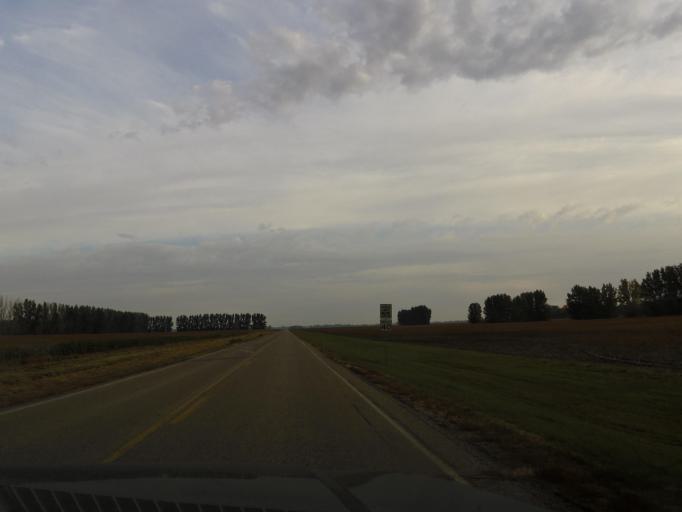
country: US
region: North Dakota
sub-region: Pembina County
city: Cavalier
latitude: 48.6885
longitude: -97.7318
